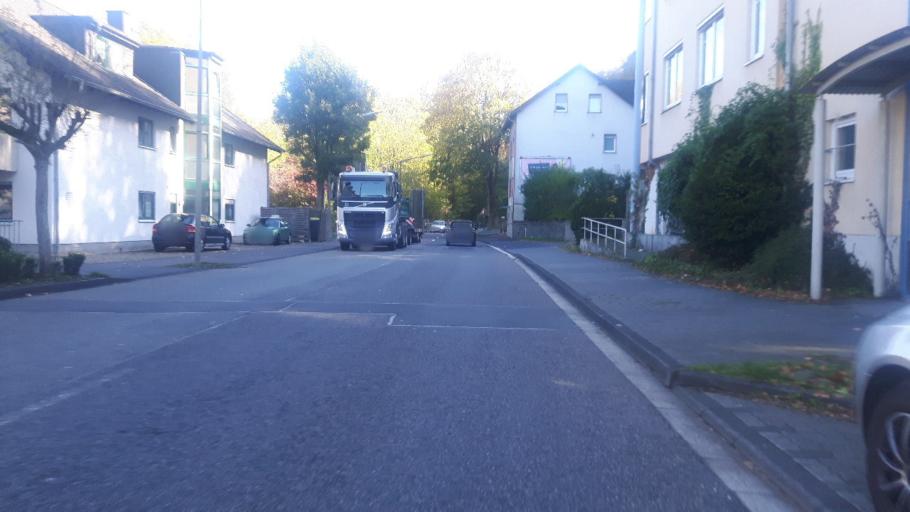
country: DE
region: Rheinland-Pfalz
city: Wissen
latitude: 50.7809
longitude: 7.7426
